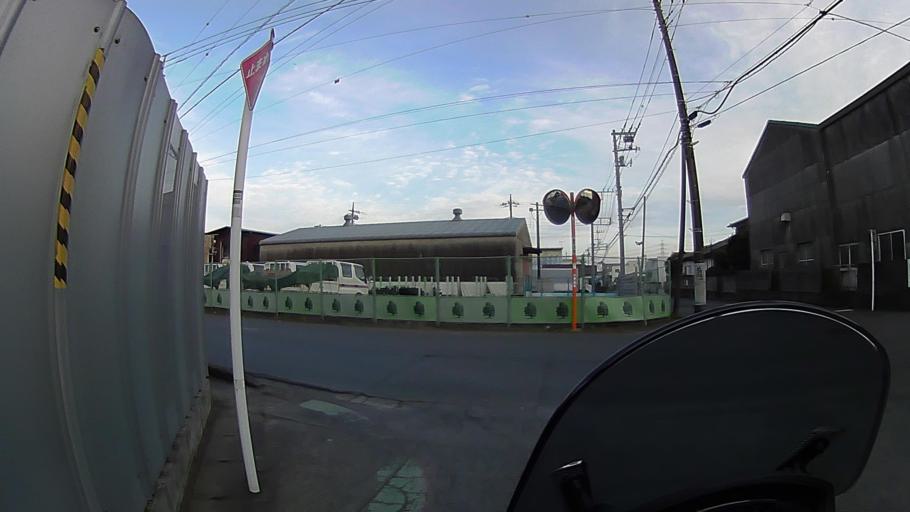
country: JP
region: Kanagawa
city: Atsugi
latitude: 35.4255
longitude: 139.4189
